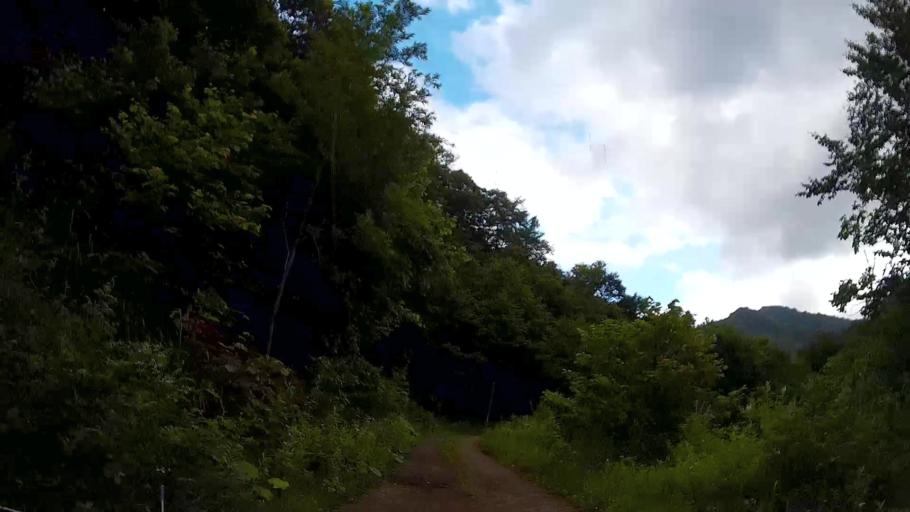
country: JP
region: Hokkaido
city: Nanae
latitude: 42.0370
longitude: 140.4828
